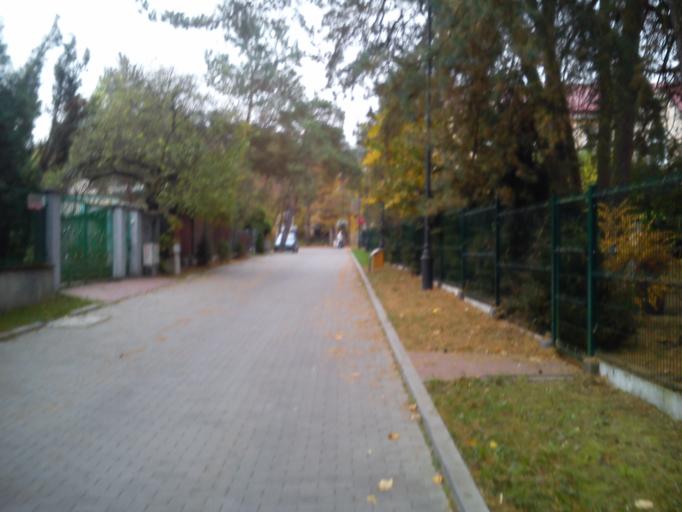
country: PL
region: Masovian Voivodeship
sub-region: Powiat piaseczynski
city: Konstancin-Jeziorna
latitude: 52.0871
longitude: 21.1197
